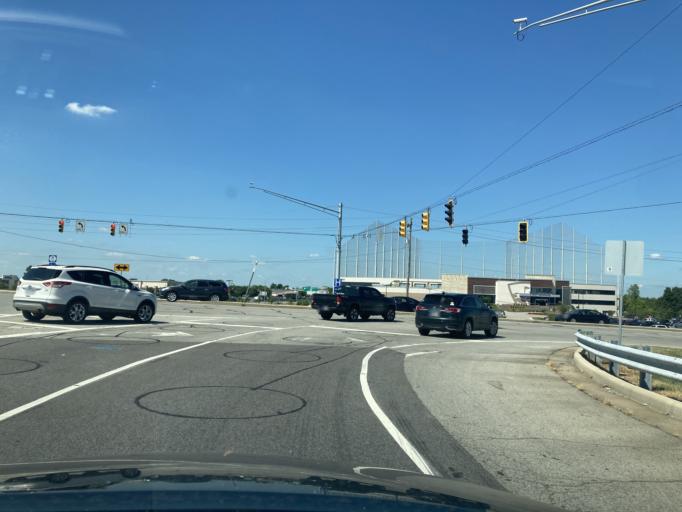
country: US
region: Indiana
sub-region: Hamilton County
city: Fishers
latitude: 39.9565
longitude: -86.0062
